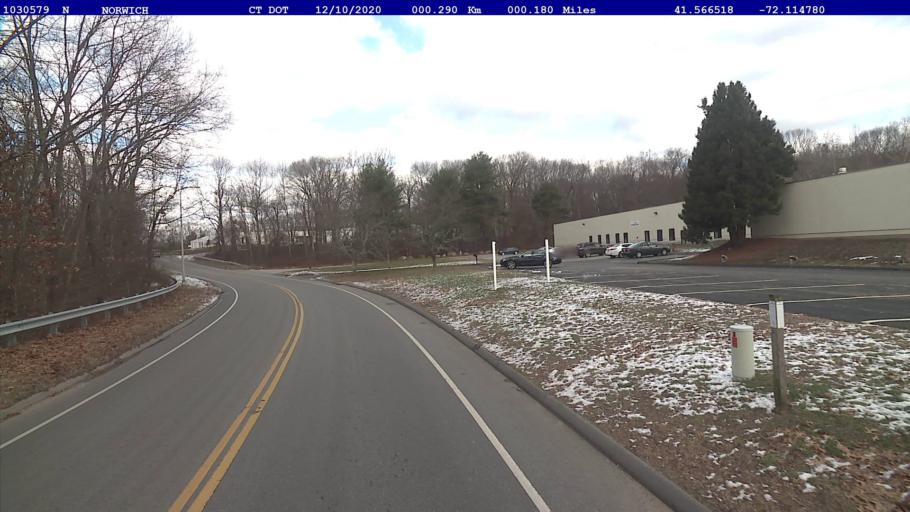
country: US
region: Connecticut
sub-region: New London County
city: Norwich
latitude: 41.5665
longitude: -72.1148
